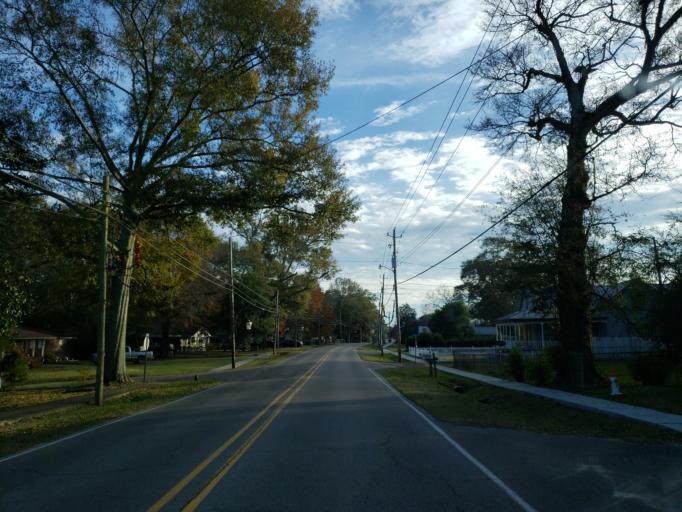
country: US
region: Mississippi
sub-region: Lamar County
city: Purvis
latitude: 31.1487
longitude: -89.4118
